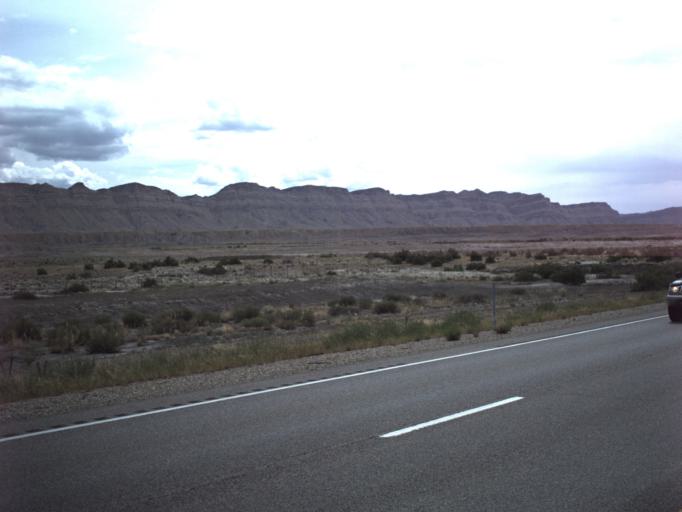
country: US
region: Utah
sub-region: Carbon County
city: East Carbon City
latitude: 39.3358
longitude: -110.3706
